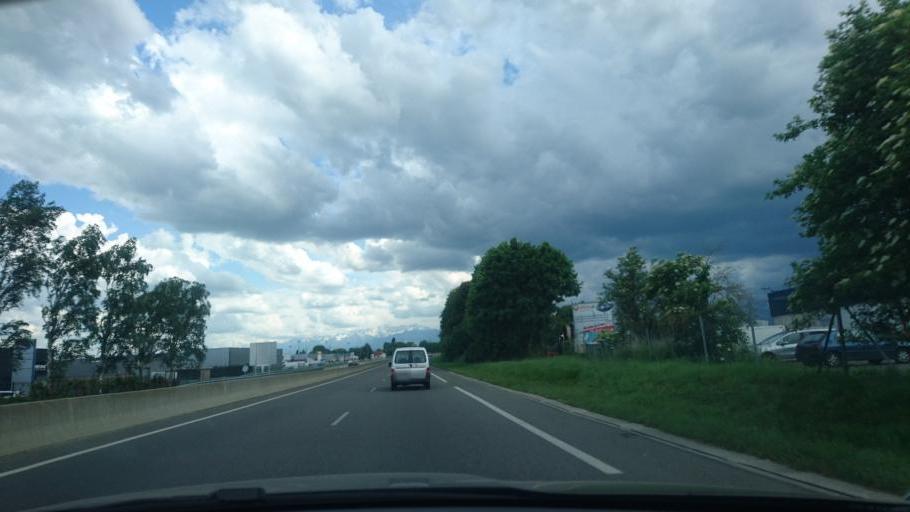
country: FR
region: Midi-Pyrenees
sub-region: Departement des Hautes-Pyrenees
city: Juillan
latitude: 43.2359
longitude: 0.0424
